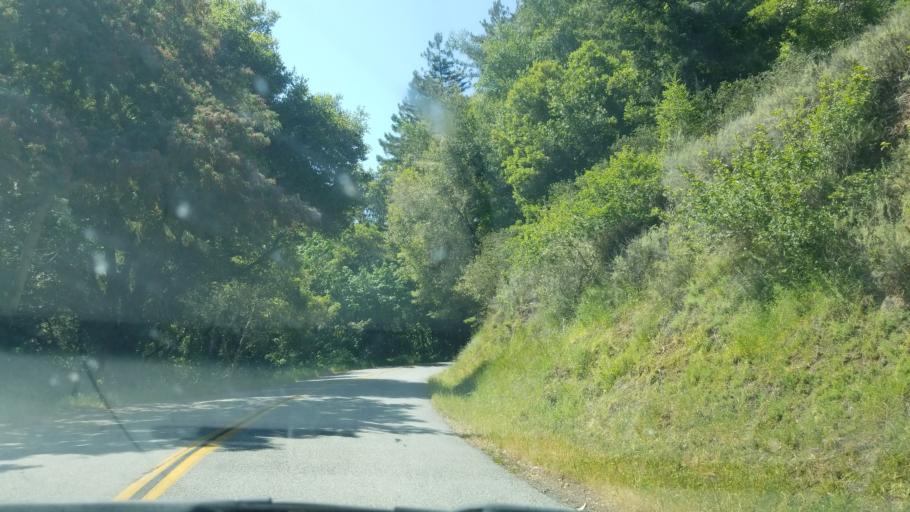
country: US
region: California
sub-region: Santa Cruz County
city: Corralitos
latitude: 37.0469
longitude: -121.8036
